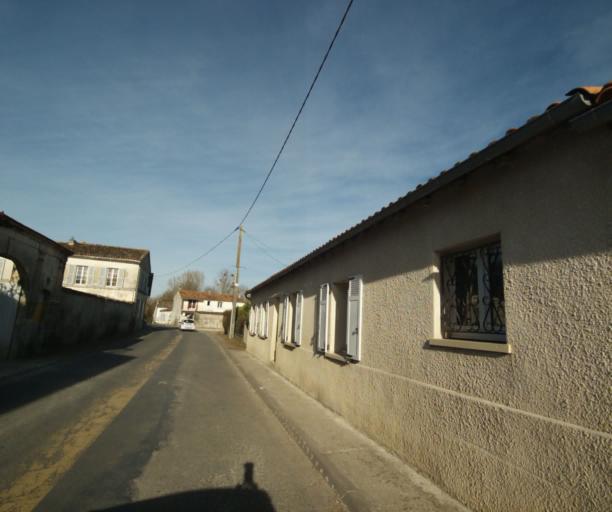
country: FR
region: Poitou-Charentes
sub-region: Departement de la Charente-Maritime
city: Chaniers
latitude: 45.7006
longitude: -0.5281
